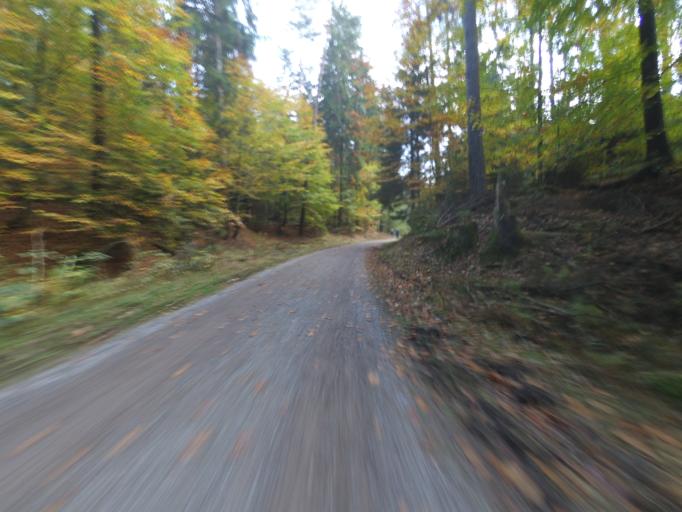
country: DE
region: Saxony
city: Albertstadt
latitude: 51.1018
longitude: 13.8197
